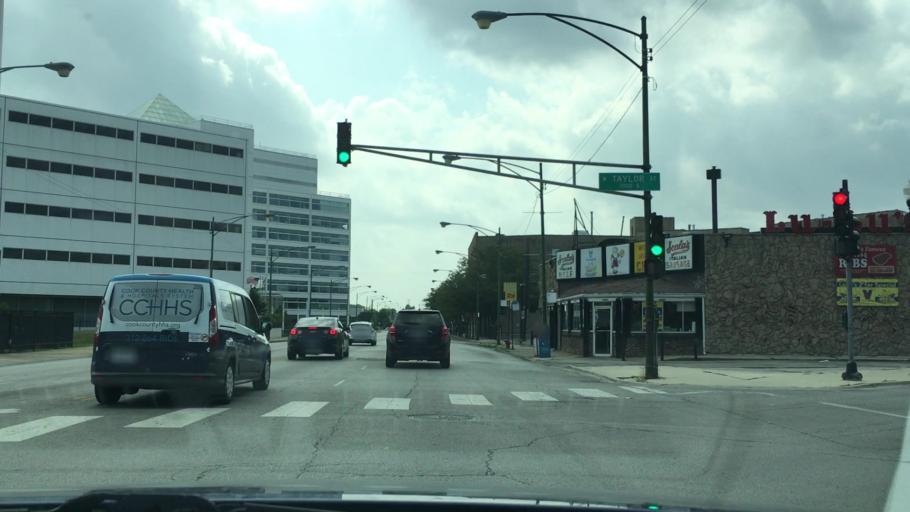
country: US
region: Illinois
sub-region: Cook County
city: Chicago
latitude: 41.8690
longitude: -87.6810
